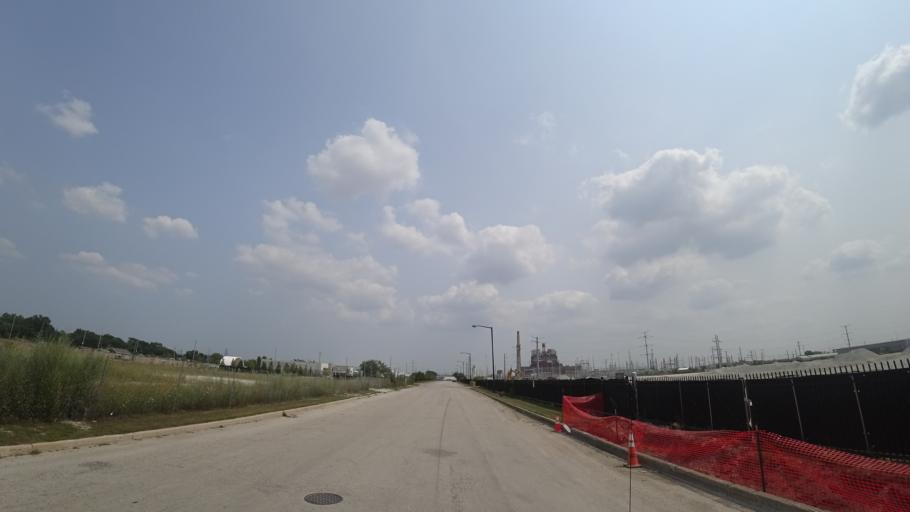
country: US
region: Illinois
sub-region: Cook County
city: Cicero
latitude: 41.8307
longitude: -87.7336
